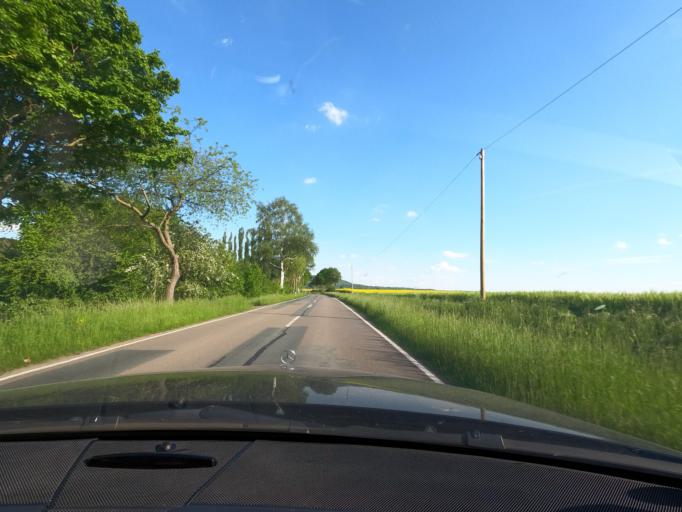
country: DE
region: Hesse
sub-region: Regierungsbezirk Kassel
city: Martinhagen
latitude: 51.3262
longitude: 9.2516
